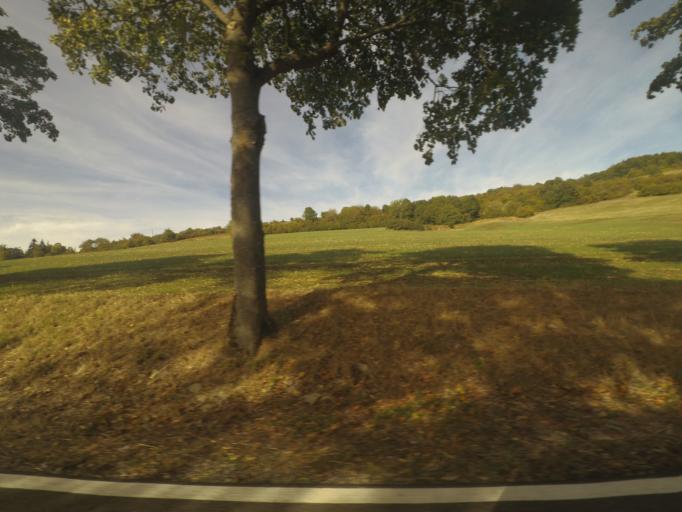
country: DE
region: Thuringia
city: Oberkatz
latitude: 50.5753
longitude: 10.2457
